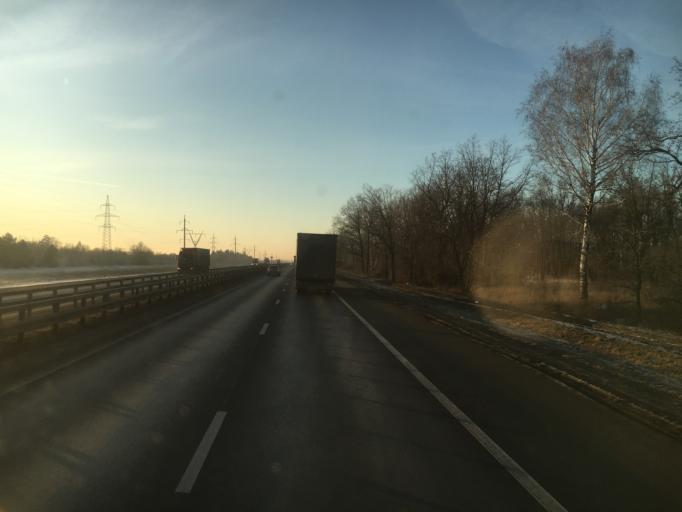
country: RU
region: Samara
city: Pribrezhnyy
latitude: 53.5184
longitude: 49.8052
